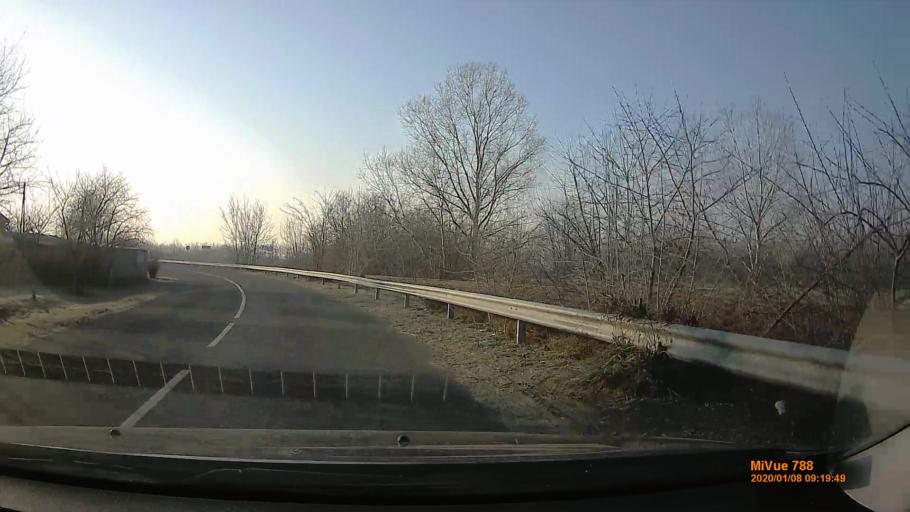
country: HU
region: Bacs-Kiskun
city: Helvecia
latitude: 46.8540
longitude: 19.6612
